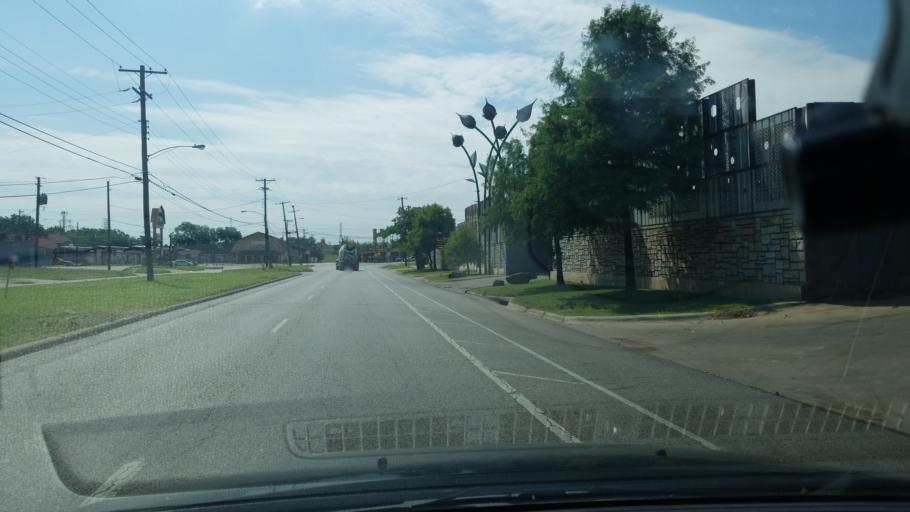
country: US
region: Texas
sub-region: Dallas County
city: Dallas
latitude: 32.7606
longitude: -96.7956
